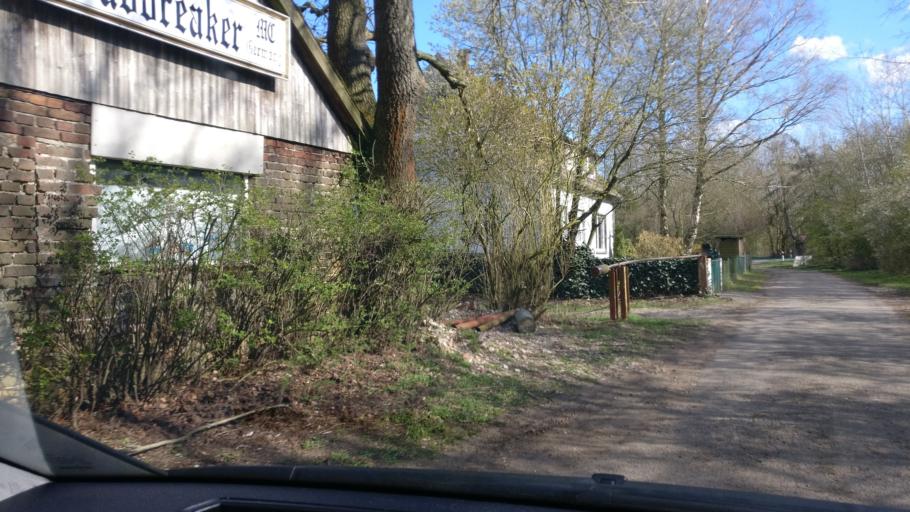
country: DE
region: North Rhine-Westphalia
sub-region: Regierungsbezirk Detmold
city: Lage
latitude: 52.0161
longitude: 8.7608
